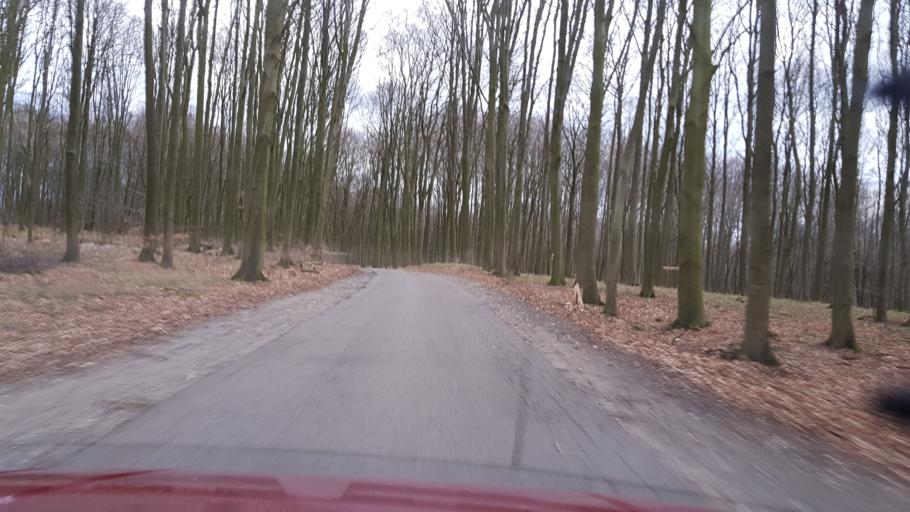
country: PL
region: West Pomeranian Voivodeship
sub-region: Szczecin
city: Szczecin
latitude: 53.3391
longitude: 14.6392
